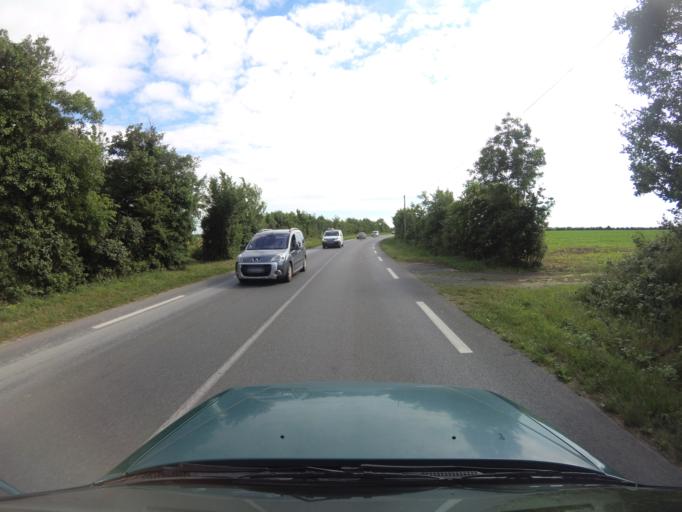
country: FR
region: Poitou-Charentes
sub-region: Departement de la Charente-Maritime
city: Saint-Xandre
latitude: 46.2205
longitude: -1.0863
